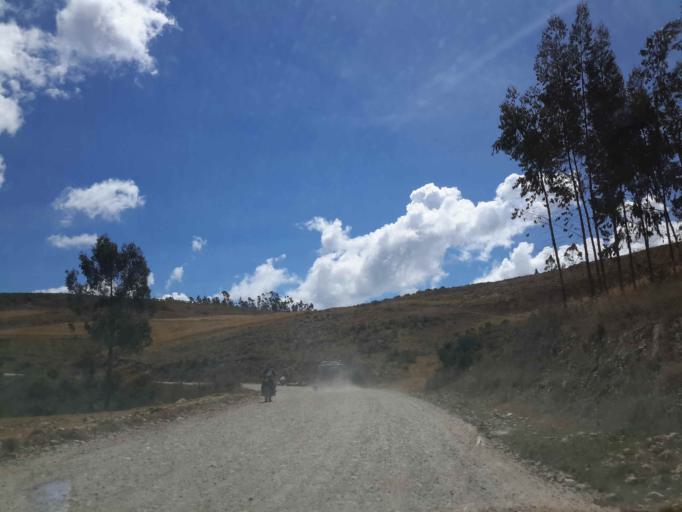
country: PE
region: Apurimac
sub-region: Provincia de Andahuaylas
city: San Jeronimo
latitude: -13.6405
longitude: -73.3340
